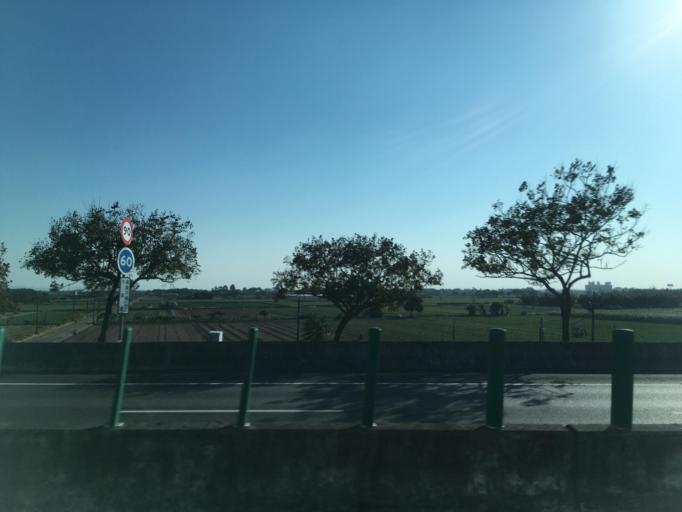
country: TW
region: Taiwan
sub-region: Chiayi
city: Taibao
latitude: 23.4225
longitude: 120.3657
